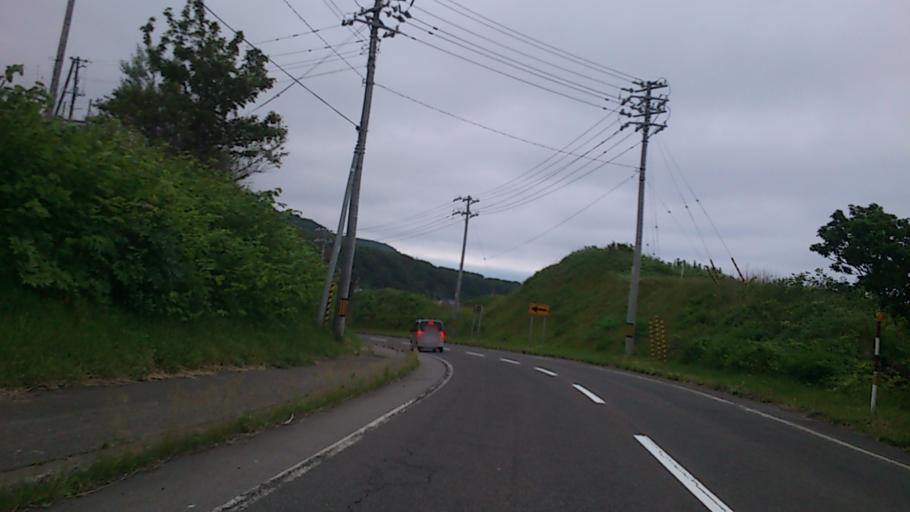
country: JP
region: Hokkaido
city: Iwanai
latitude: 42.7340
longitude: 140.0914
